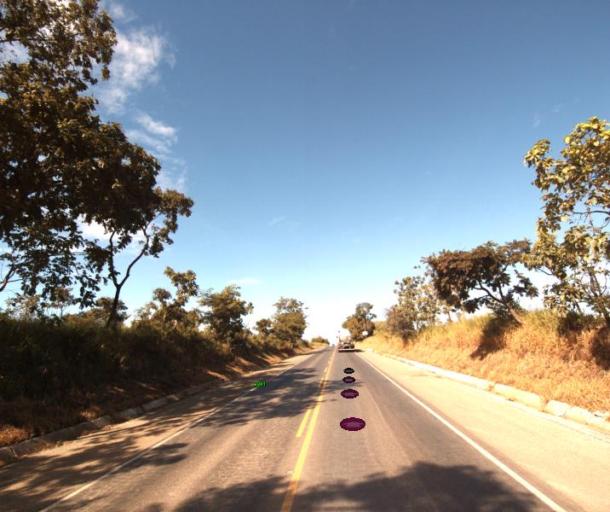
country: BR
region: Goias
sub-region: Itapaci
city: Itapaci
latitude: -14.8513
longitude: -49.3173
